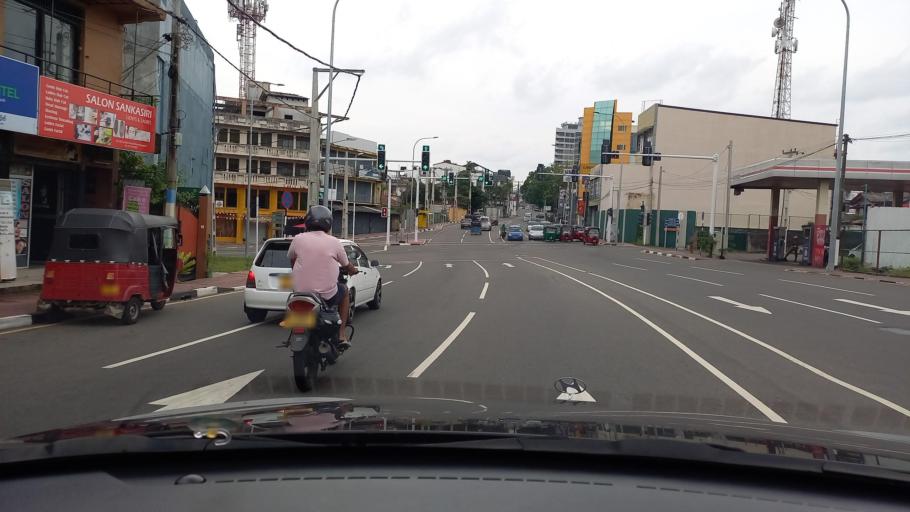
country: LK
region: Western
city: Sri Jayewardenepura Kotte
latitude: 6.8758
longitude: 79.9008
